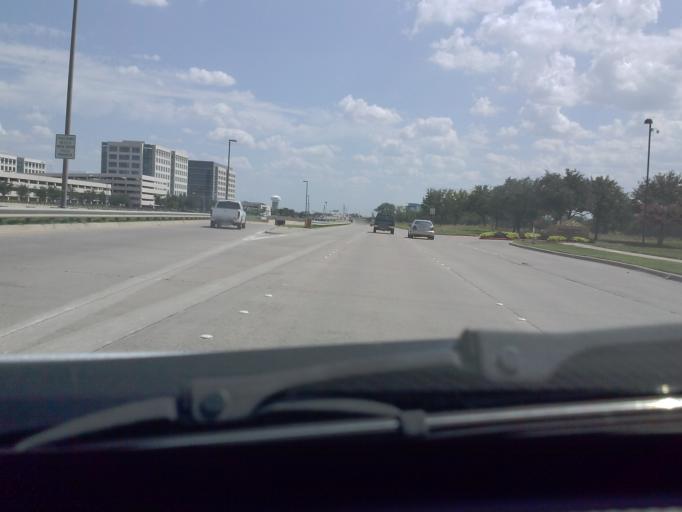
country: US
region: Texas
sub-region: Denton County
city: The Colony
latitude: 33.0767
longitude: -96.8251
